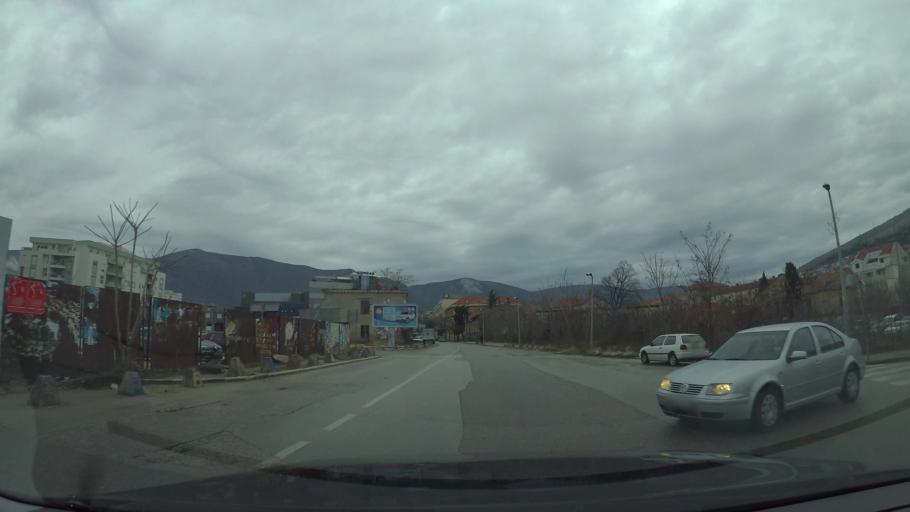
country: BA
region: Federation of Bosnia and Herzegovina
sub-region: Hercegovacko-Bosanski Kanton
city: Mostar
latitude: 43.3446
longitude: 17.8077
